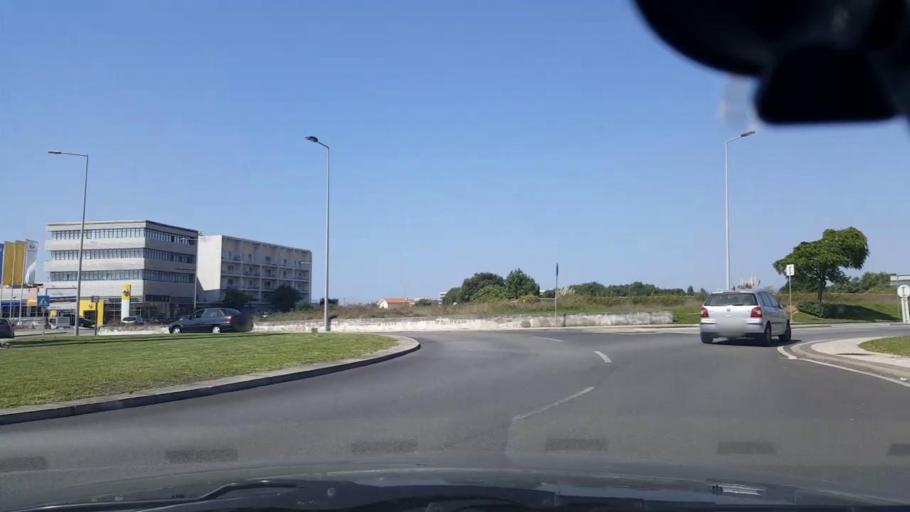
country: PT
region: Porto
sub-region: Vila do Conde
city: Vila do Conde
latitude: 41.3649
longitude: -8.7415
